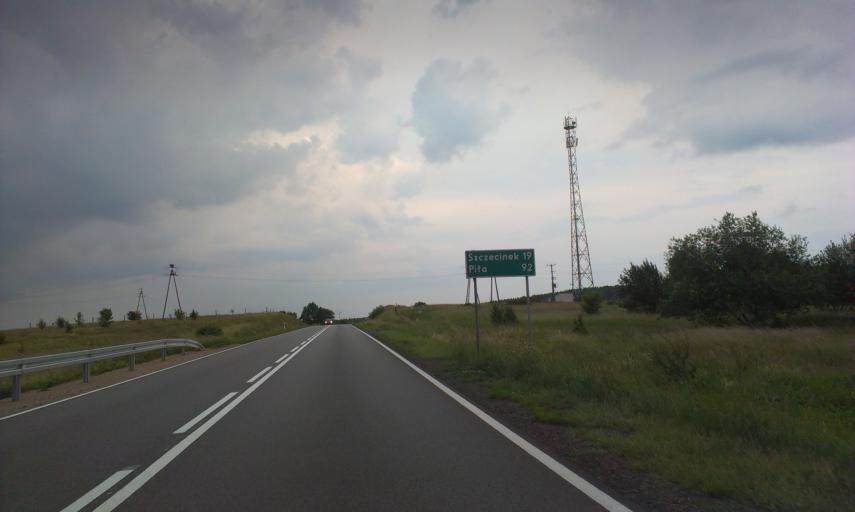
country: PL
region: West Pomeranian Voivodeship
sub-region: Powiat koszalinski
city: Bobolice
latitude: 53.8547
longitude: 16.6121
